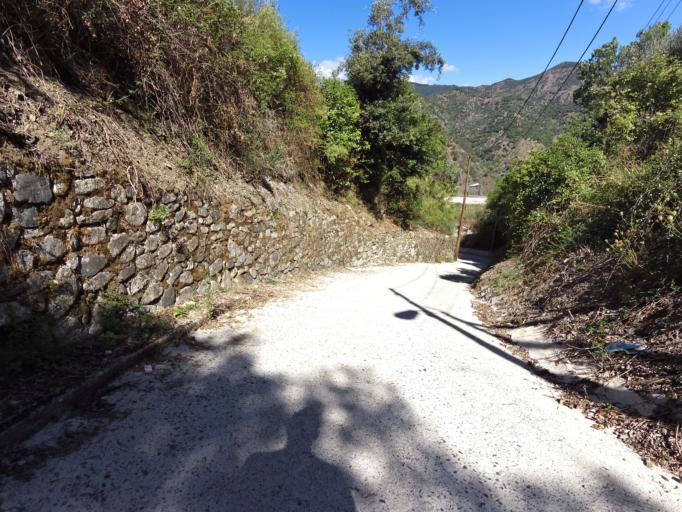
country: IT
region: Calabria
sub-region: Provincia di Reggio Calabria
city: Pazzano
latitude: 38.4795
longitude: 16.4515
